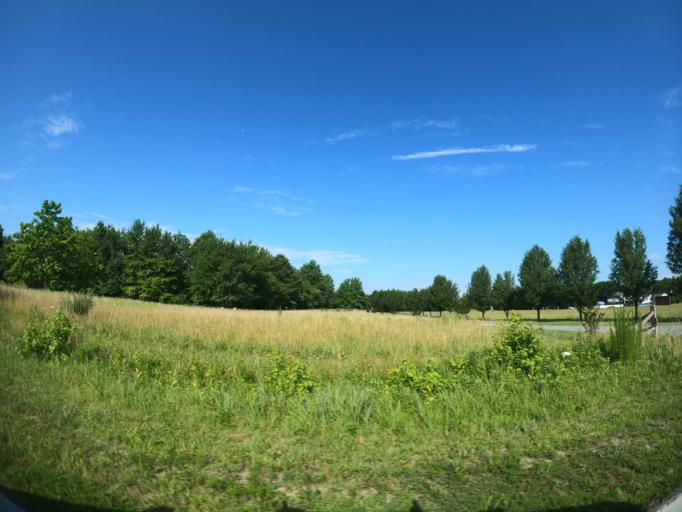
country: US
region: Delaware
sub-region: Sussex County
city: Ocean View
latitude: 38.4856
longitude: -75.1180
